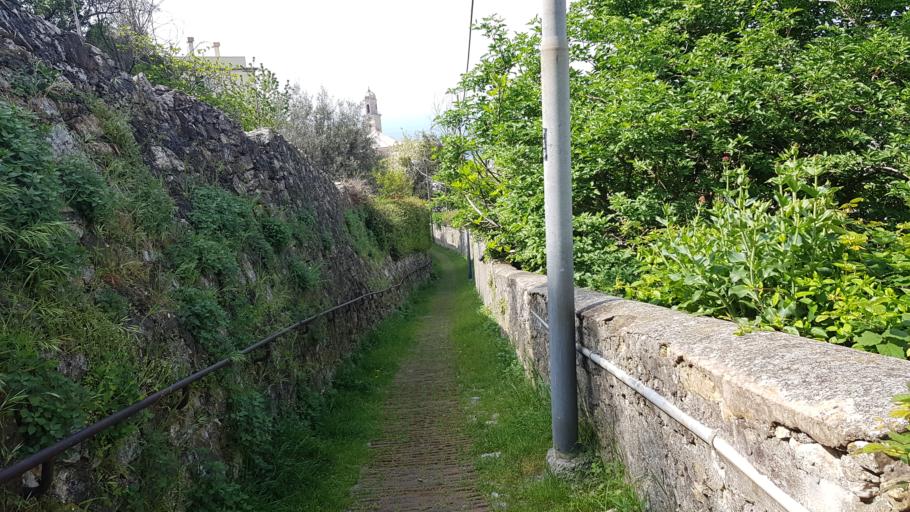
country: IT
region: Liguria
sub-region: Provincia di Genova
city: Genoa
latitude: 44.4231
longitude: 8.9330
